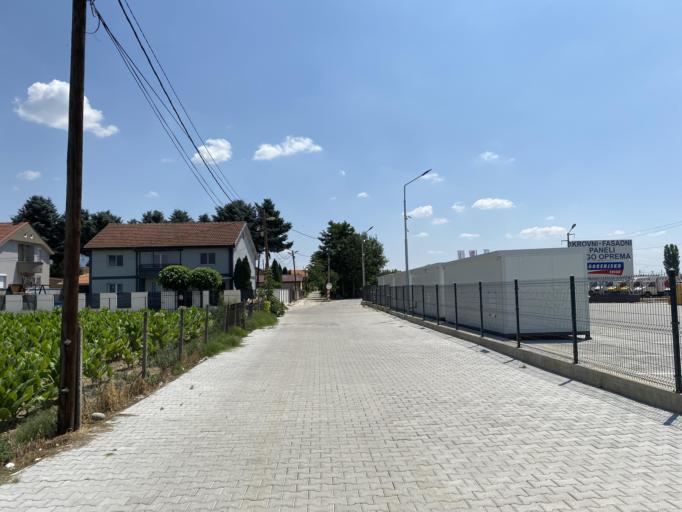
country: MK
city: Radishani
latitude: 42.0466
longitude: 21.4465
